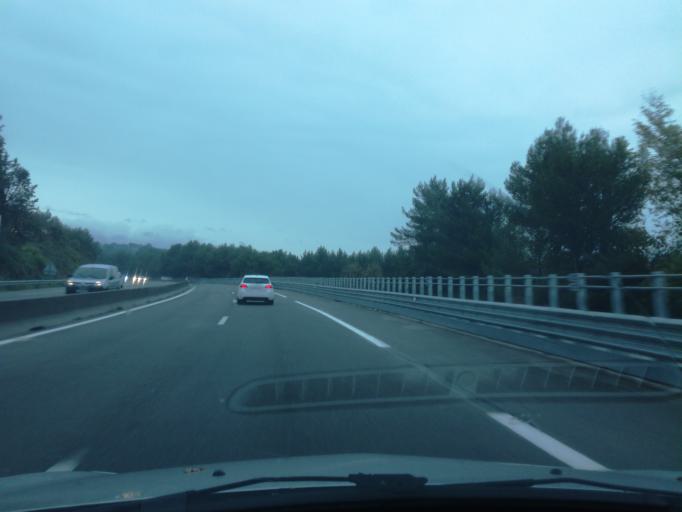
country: FR
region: Provence-Alpes-Cote d'Azur
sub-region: Departement des Alpes-Maritimes
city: Mougins
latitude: 43.6018
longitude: 7.0027
